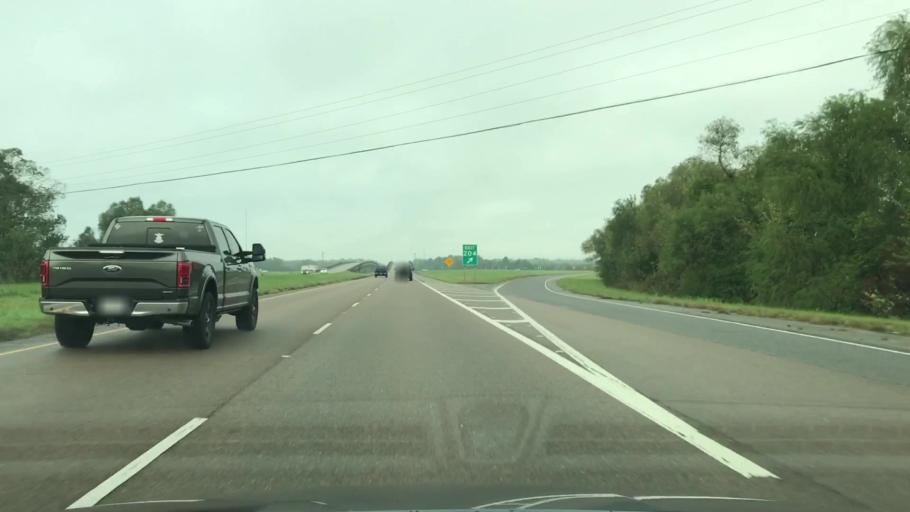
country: US
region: Louisiana
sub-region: Terrebonne Parish
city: Gray
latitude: 29.6834
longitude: -90.7438
